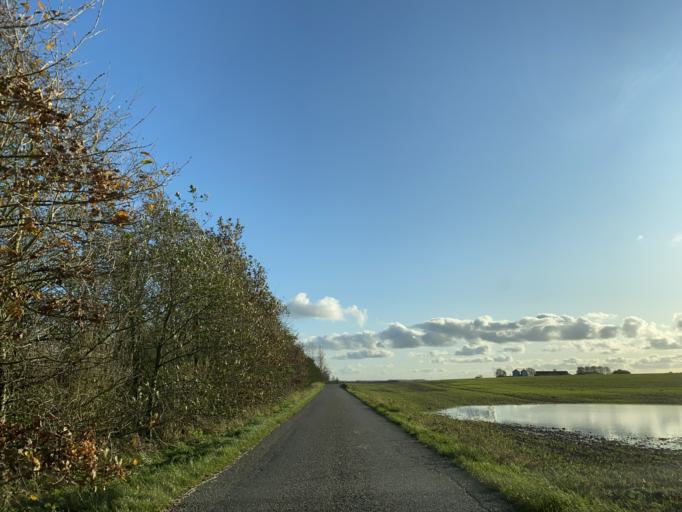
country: DK
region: Central Jutland
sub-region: Viborg Kommune
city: Bjerringbro
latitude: 56.3401
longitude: 9.7147
